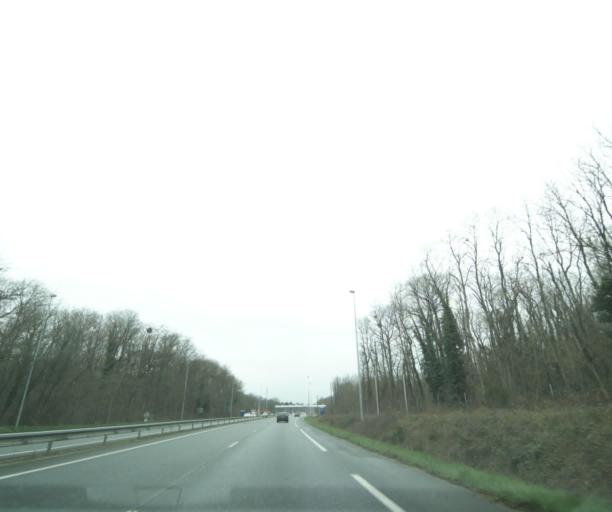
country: FR
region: Centre
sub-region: Departement du Loiret
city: Olivet
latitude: 47.8404
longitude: 1.8733
